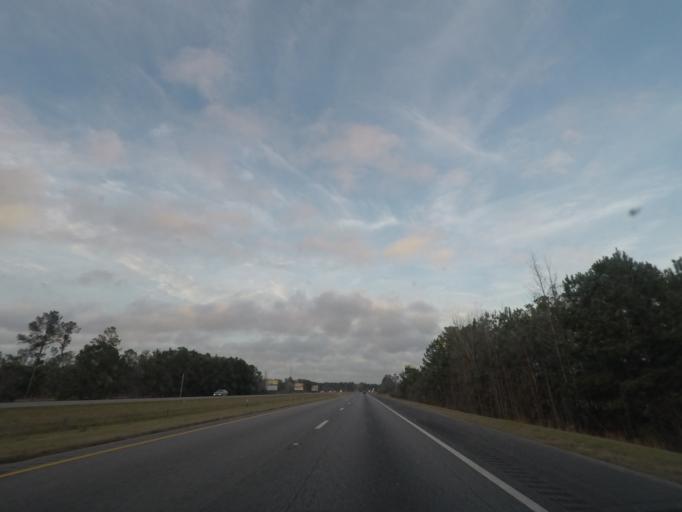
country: US
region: South Carolina
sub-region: Orangeburg County
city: Holly Hill
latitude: 33.3914
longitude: -80.5152
